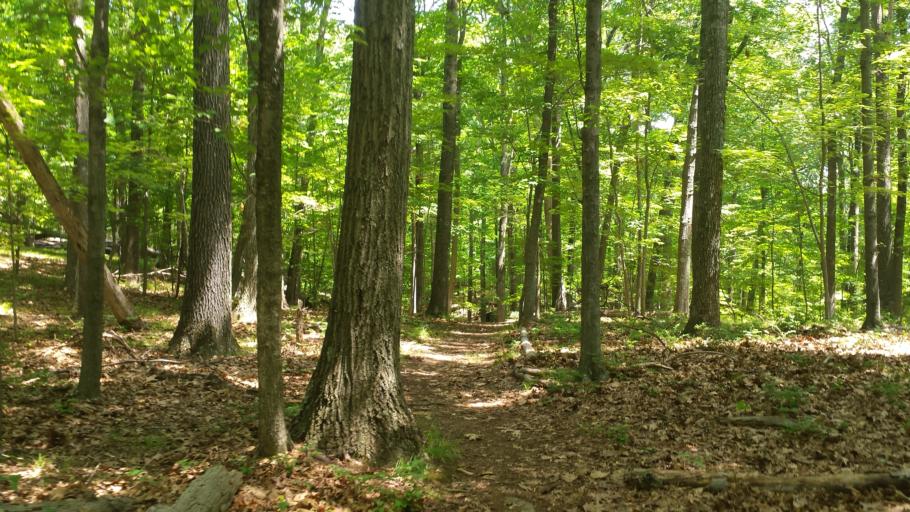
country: US
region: New York
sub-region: Westchester County
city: Yorktown Heights
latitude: 41.2204
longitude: -73.7816
